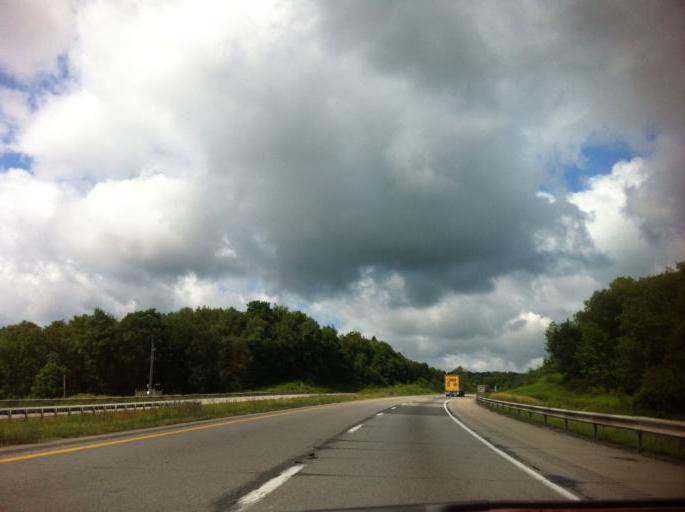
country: US
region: Pennsylvania
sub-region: Lawrence County
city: New Wilmington
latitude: 41.1816
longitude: -80.3088
